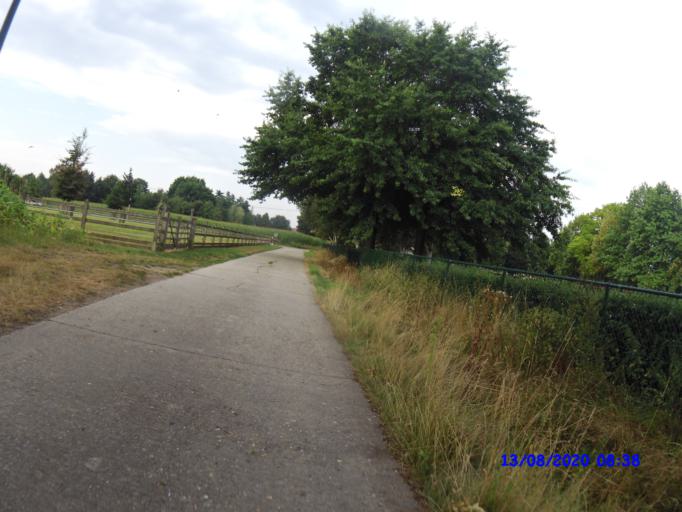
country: BE
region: Flanders
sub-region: Provincie Antwerpen
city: Brecht
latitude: 51.3506
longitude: 4.6890
